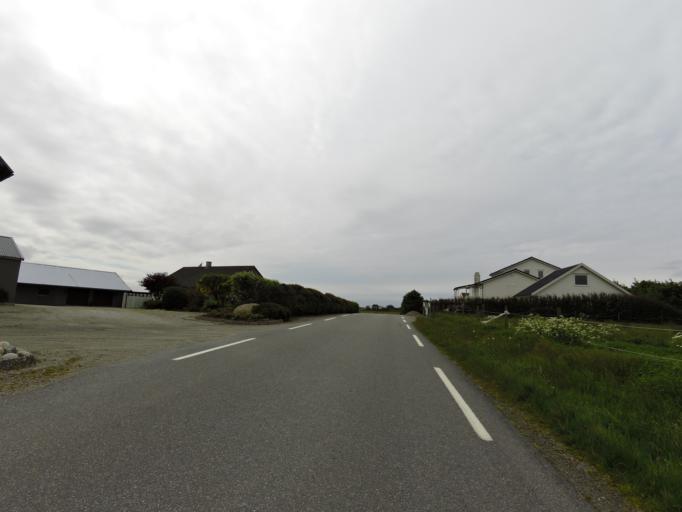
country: NO
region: Rogaland
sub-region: Klepp
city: Kleppe
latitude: 58.8153
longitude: 5.5574
